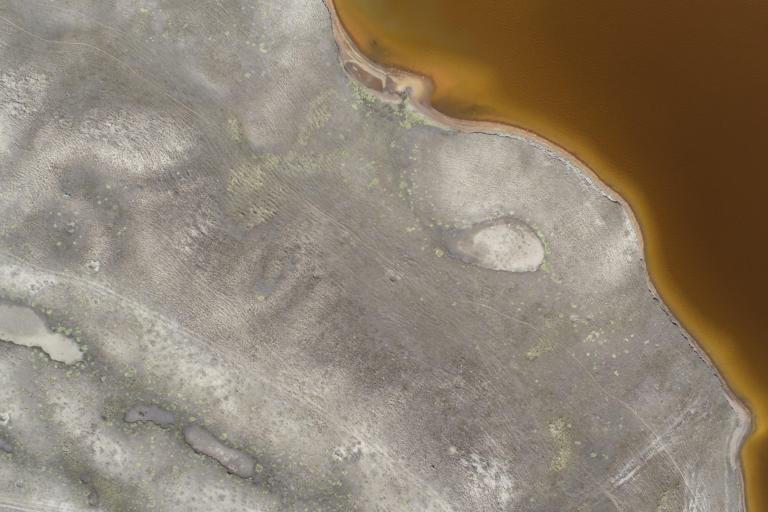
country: BO
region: La Paz
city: La Paz
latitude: -16.3449
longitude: -68.1616
